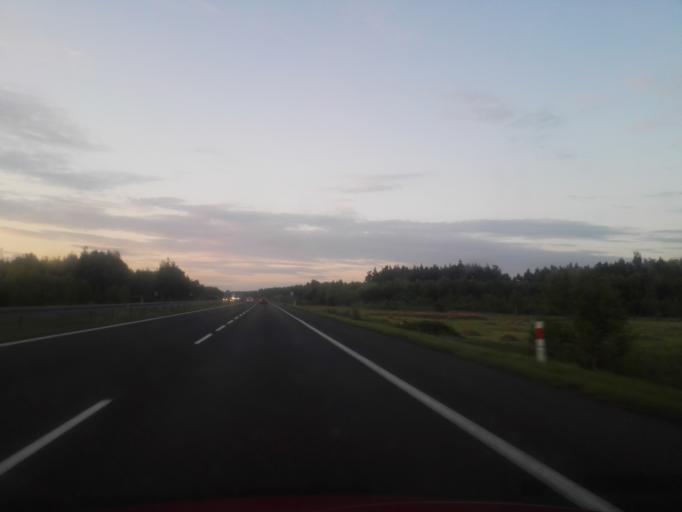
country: PL
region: Lodz Voivodeship
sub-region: Powiat radomszczanski
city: Radomsko
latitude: 51.0530
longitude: 19.3558
